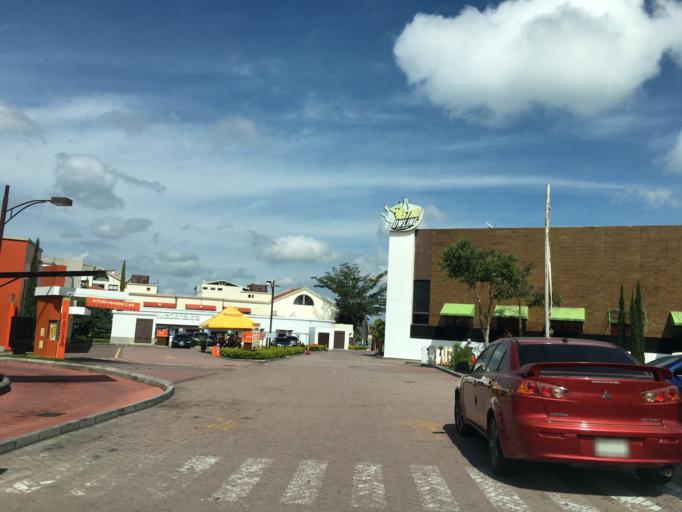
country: GT
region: Guatemala
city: Guatemala City
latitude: 14.6105
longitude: -90.4829
